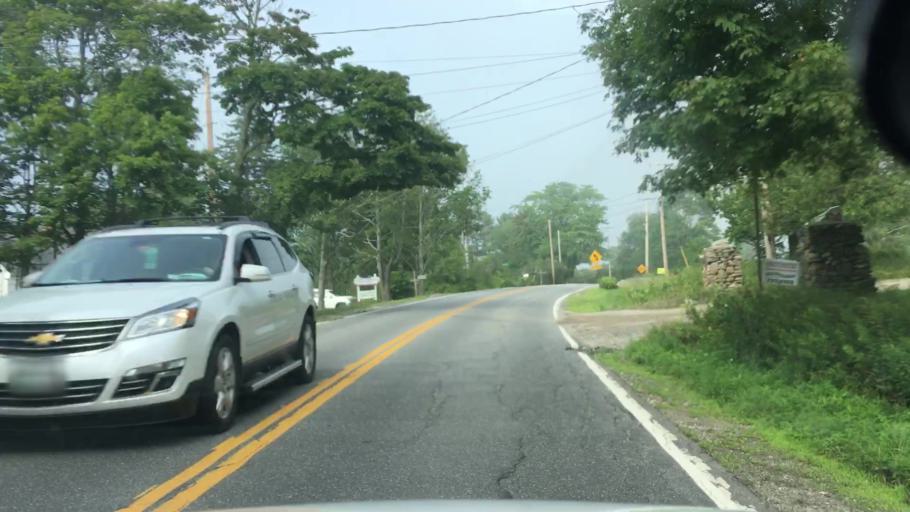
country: US
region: Maine
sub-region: Cumberland County
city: Harpswell Center
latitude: 43.7658
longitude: -69.9735
